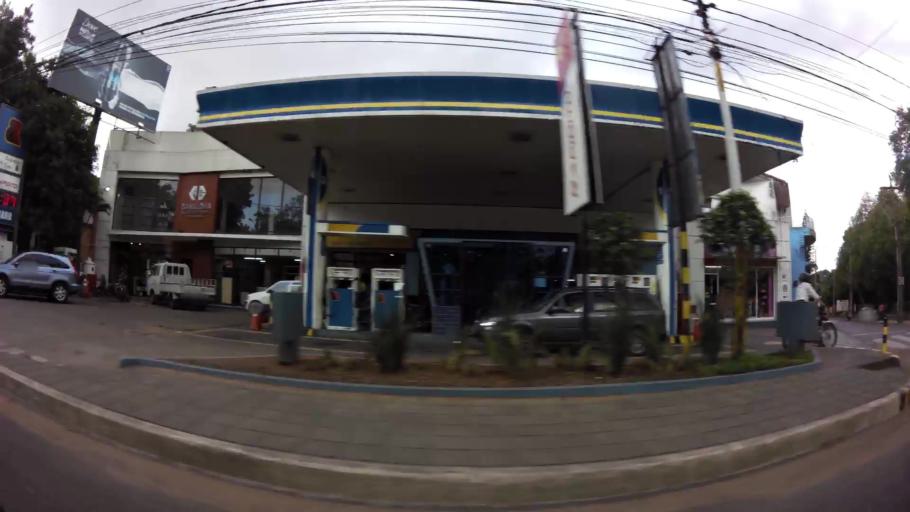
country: PY
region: Asuncion
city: Asuncion
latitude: -25.2901
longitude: -57.5924
